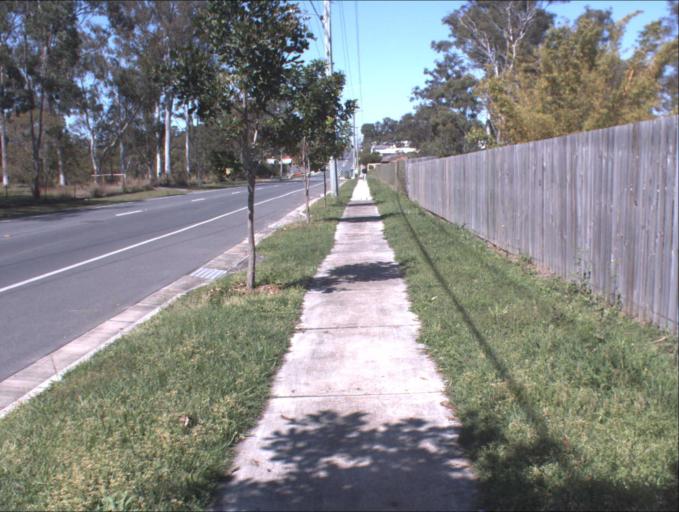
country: AU
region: Queensland
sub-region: Logan
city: Logan City
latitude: -27.6708
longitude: 153.0948
